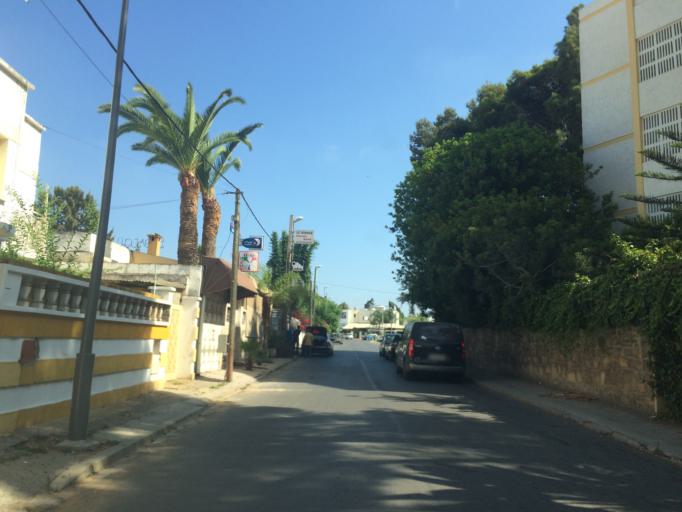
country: MA
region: Rabat-Sale-Zemmour-Zaer
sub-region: Rabat
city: Rabat
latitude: 33.9918
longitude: -6.8261
